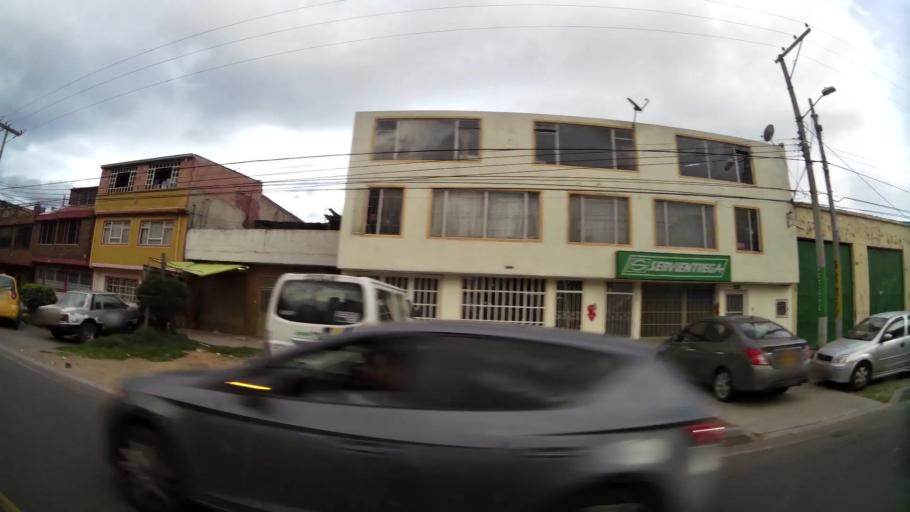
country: CO
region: Bogota D.C.
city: Bogota
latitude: 4.5949
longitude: -74.1307
